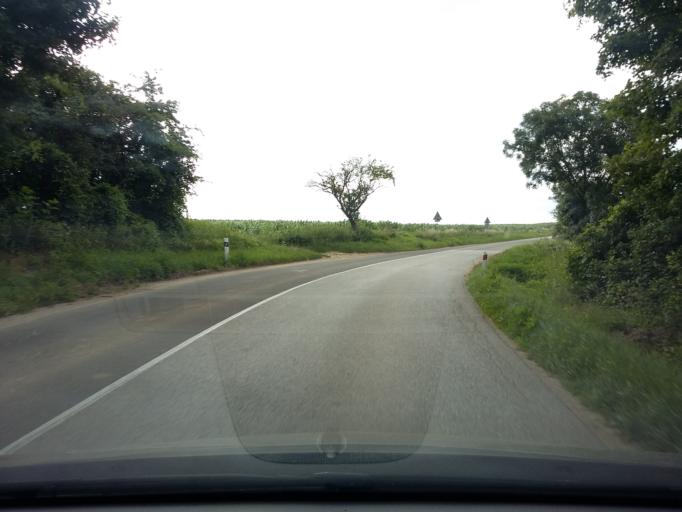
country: SK
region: Trnavsky
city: Smolenice
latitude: 48.5356
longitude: 17.4466
